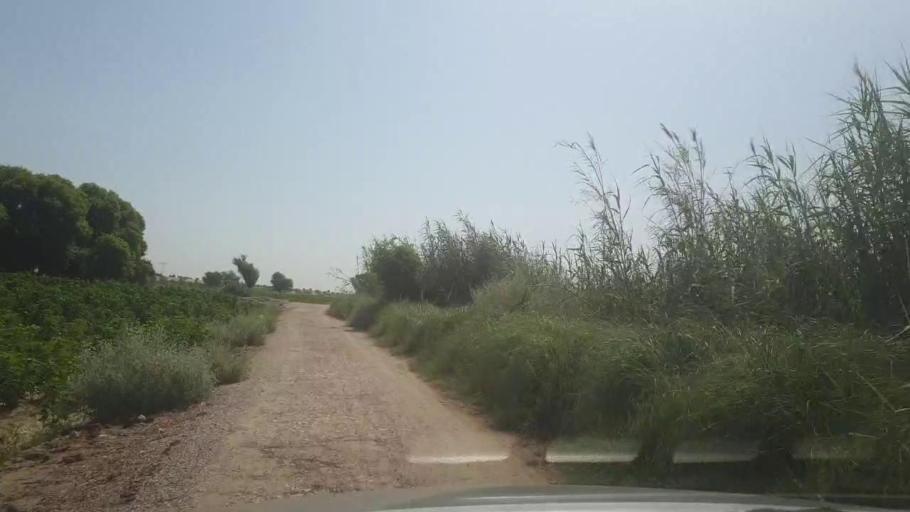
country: PK
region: Sindh
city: Rohri
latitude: 27.4108
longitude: 69.0920
